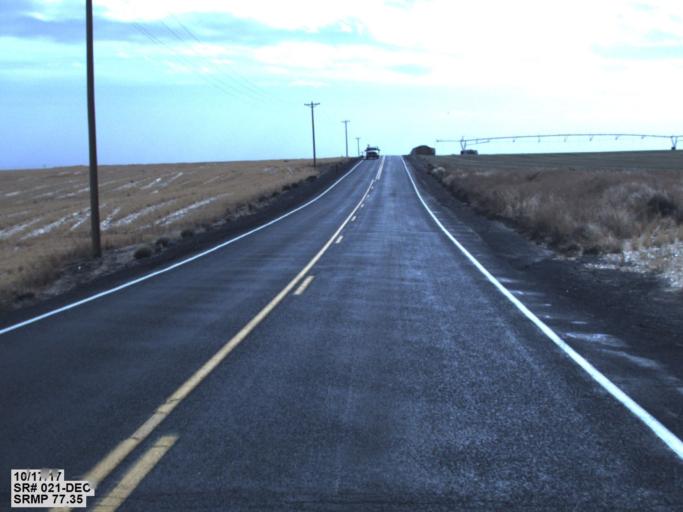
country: US
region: Washington
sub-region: Okanogan County
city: Coulee Dam
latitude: 47.6013
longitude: -118.7861
